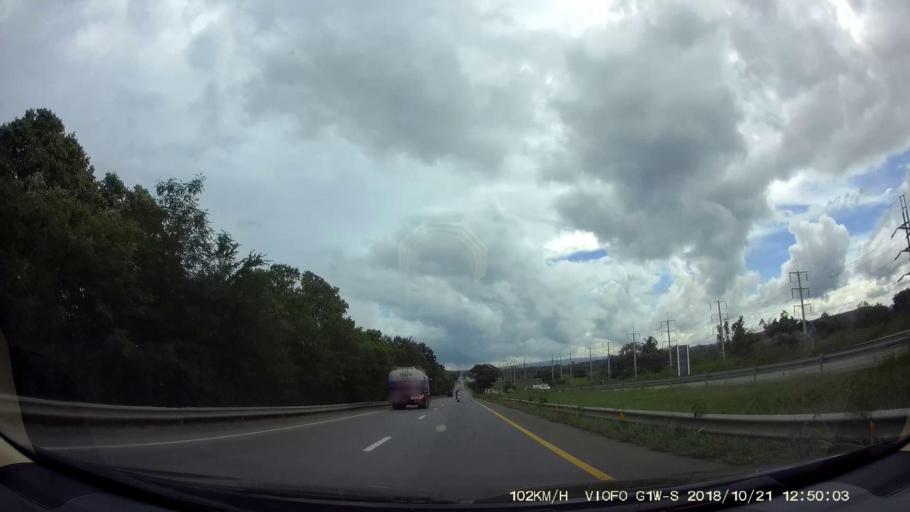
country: TH
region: Nakhon Ratchasima
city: Amphoe Sikhiu
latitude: 14.8878
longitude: 101.6878
